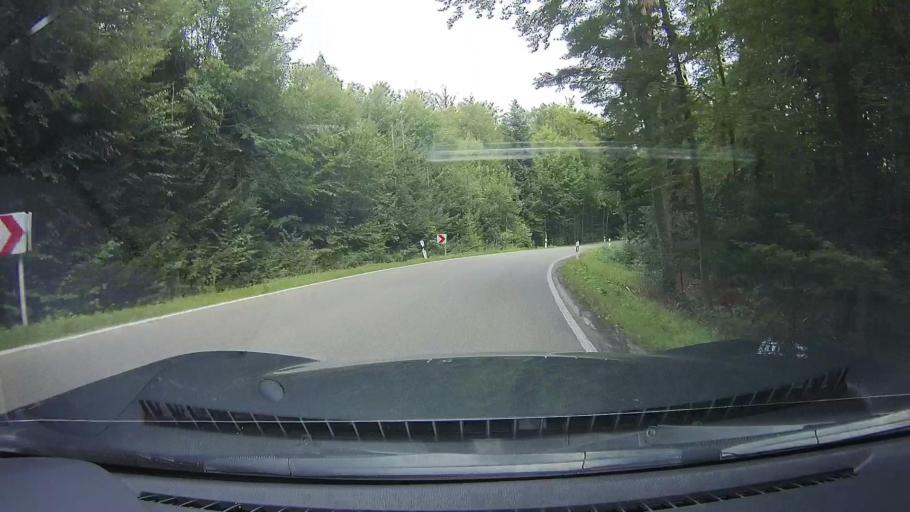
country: DE
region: Baden-Wuerttemberg
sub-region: Regierungsbezirk Stuttgart
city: Kaisersbach
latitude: 48.9408
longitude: 9.6074
